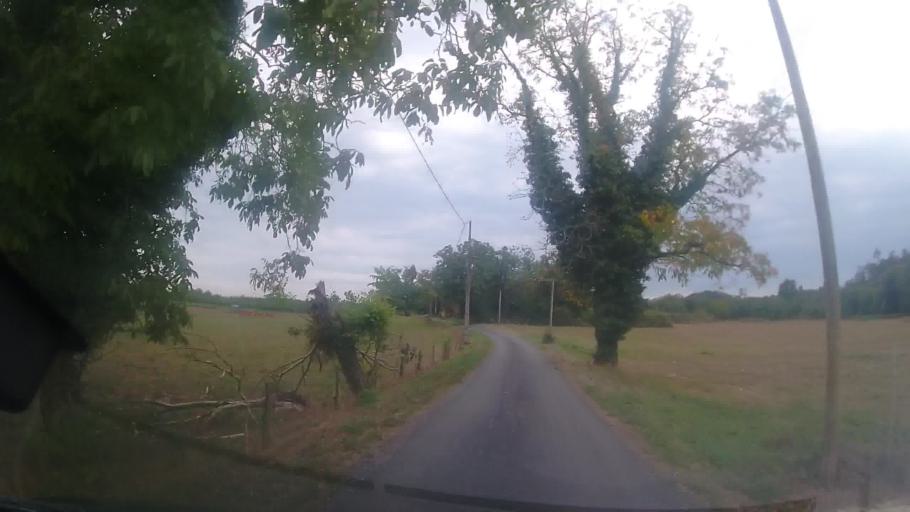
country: FR
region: Aquitaine
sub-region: Departement de la Dordogne
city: Eyvigues-et-Eybenes
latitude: 44.8386
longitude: 1.3567
